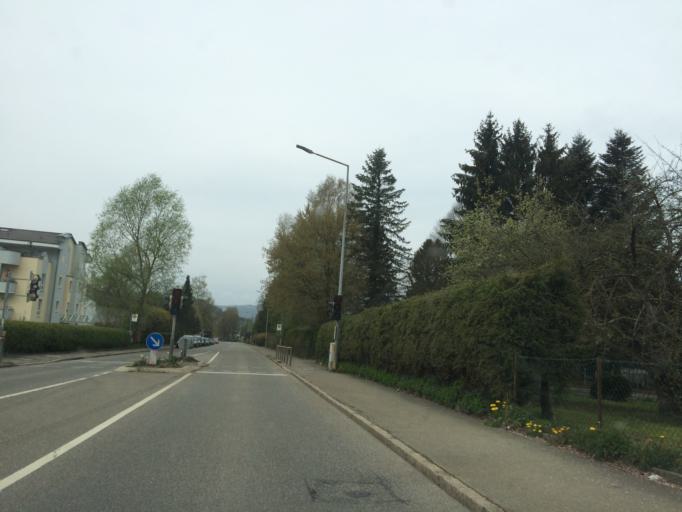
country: DE
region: Baden-Wuerttemberg
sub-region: Freiburg Region
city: Tuttlingen
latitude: 47.9812
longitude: 8.8446
